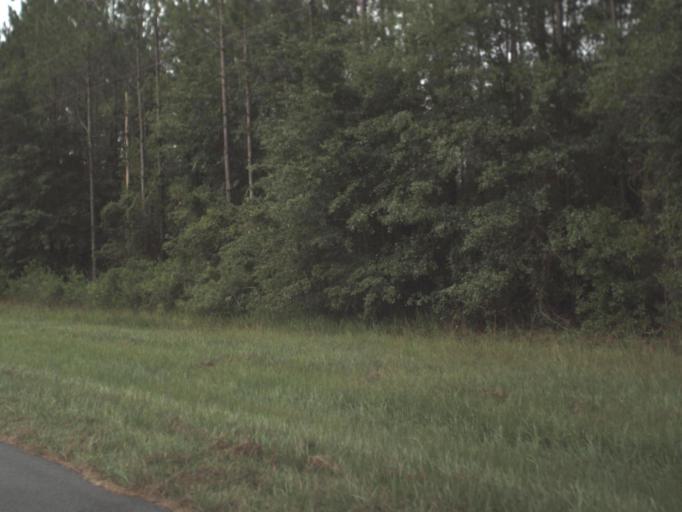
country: US
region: Florida
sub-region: Columbia County
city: Five Points
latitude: 30.4845
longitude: -82.6602
